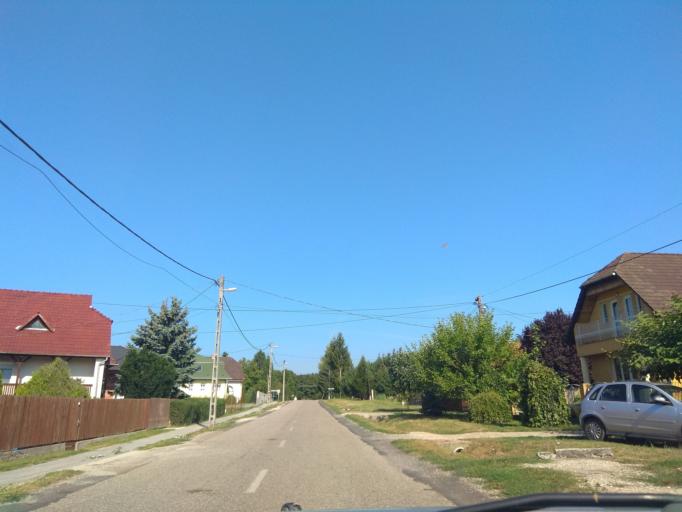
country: HU
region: Borsod-Abauj-Zemplen
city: Harsany
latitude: 47.9927
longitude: 20.7656
